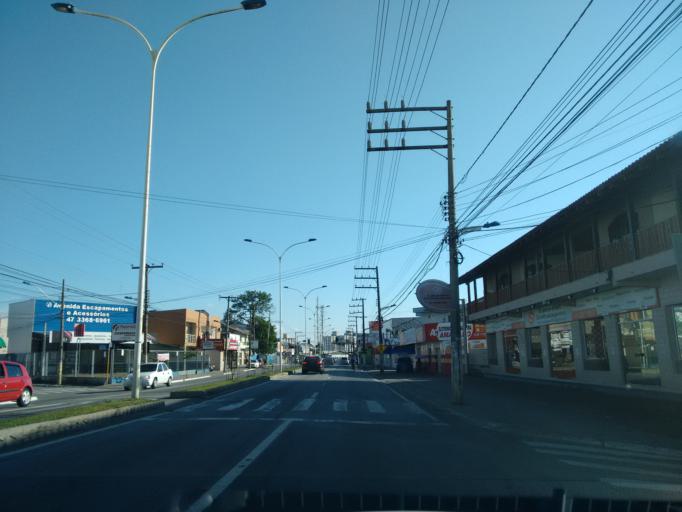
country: BR
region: Santa Catarina
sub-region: Itajai
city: Itajai
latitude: -26.8856
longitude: -48.6970
